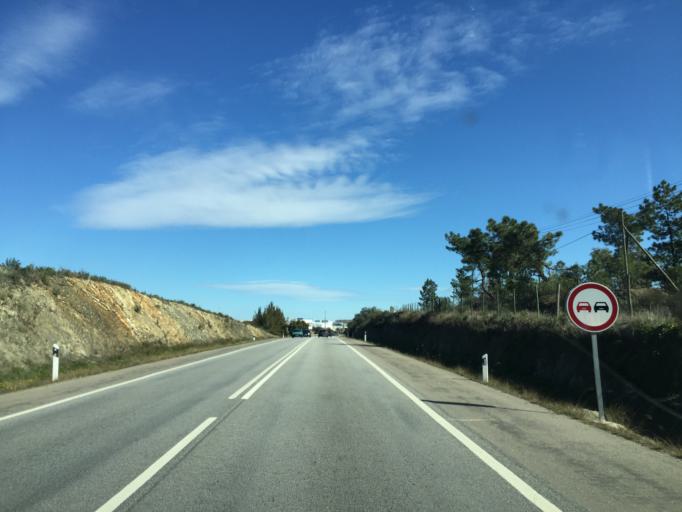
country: PT
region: Castelo Branco
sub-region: Castelo Branco
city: Castelo Branco
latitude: 39.8022
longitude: -7.5261
